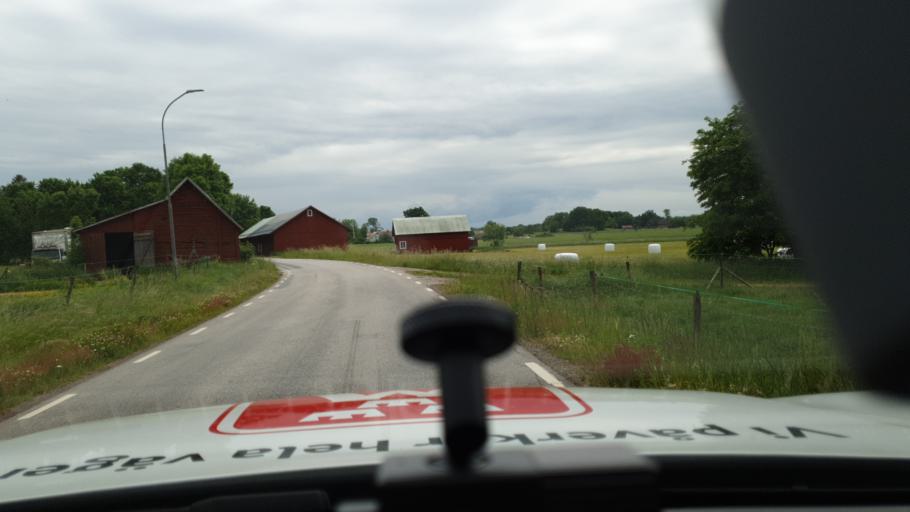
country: SE
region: Vaestra Goetaland
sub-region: Mariestads Kommun
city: Mariestad
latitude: 58.6009
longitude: 13.8660
